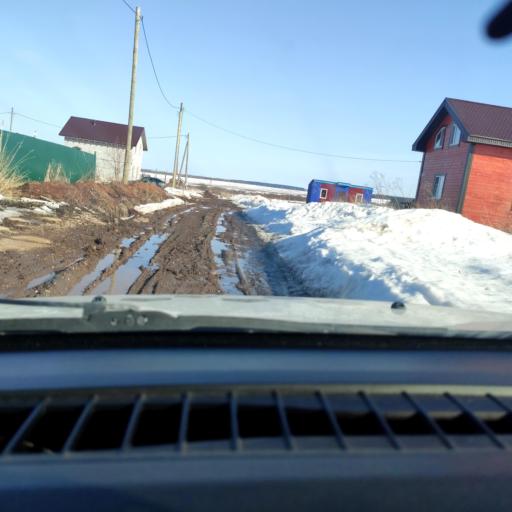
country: RU
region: Perm
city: Kultayevo
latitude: 57.8712
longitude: 55.9771
